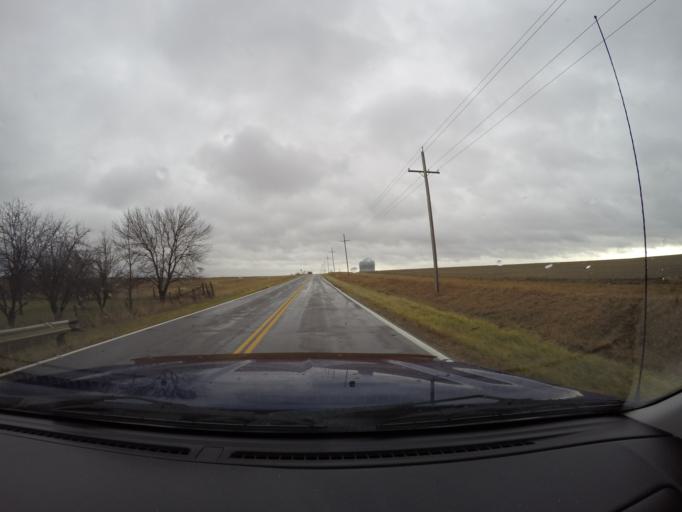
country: US
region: Kansas
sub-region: Jefferson County
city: Oskaloosa
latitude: 39.3394
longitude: -95.3293
